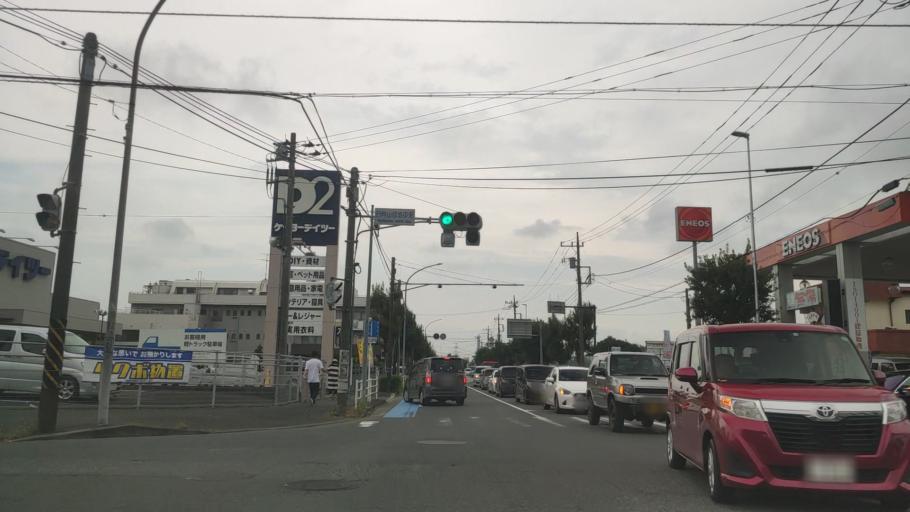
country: JP
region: Kanagawa
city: Minami-rinkan
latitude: 35.4429
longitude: 139.4844
